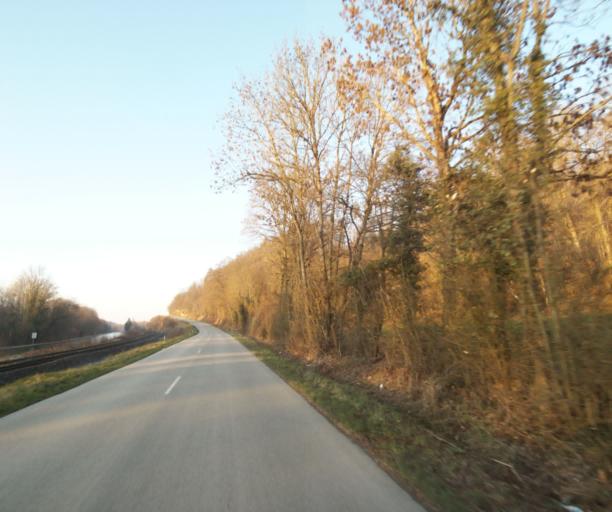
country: FR
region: Champagne-Ardenne
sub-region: Departement de la Haute-Marne
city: Bienville
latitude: 48.5862
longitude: 5.0447
